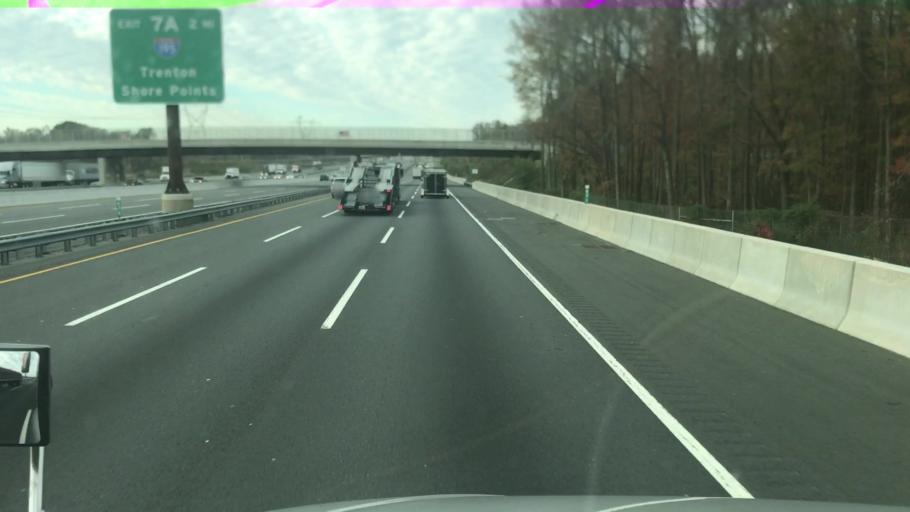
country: US
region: New Jersey
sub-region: Monmouth County
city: Allentown
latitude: 40.2218
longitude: -74.5605
